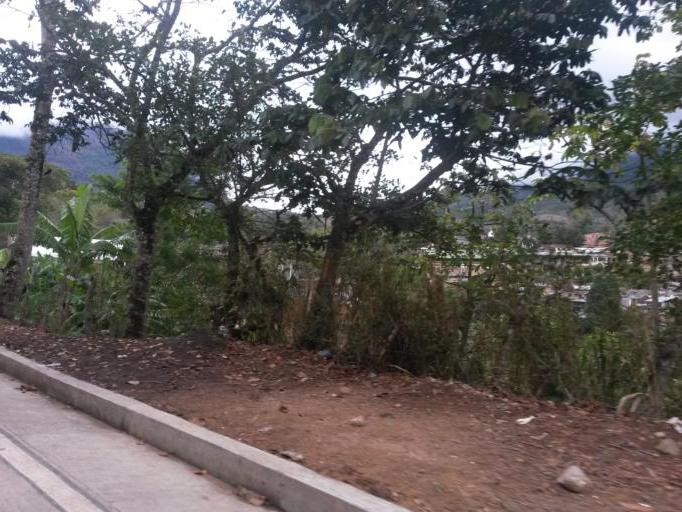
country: CO
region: Cauca
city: Almaguer
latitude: 1.8327
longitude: -76.9706
